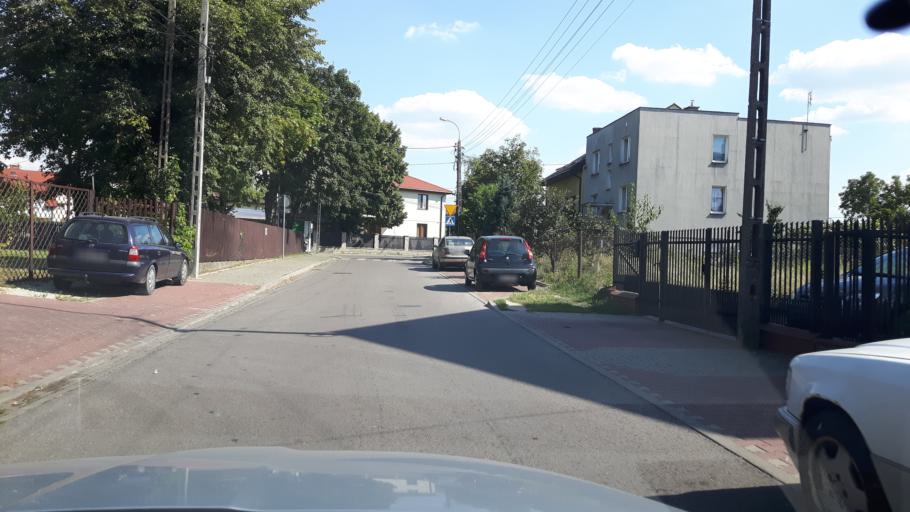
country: PL
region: Masovian Voivodeship
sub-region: Powiat pruszkowski
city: Raszyn
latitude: 52.1581
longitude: 20.9306
